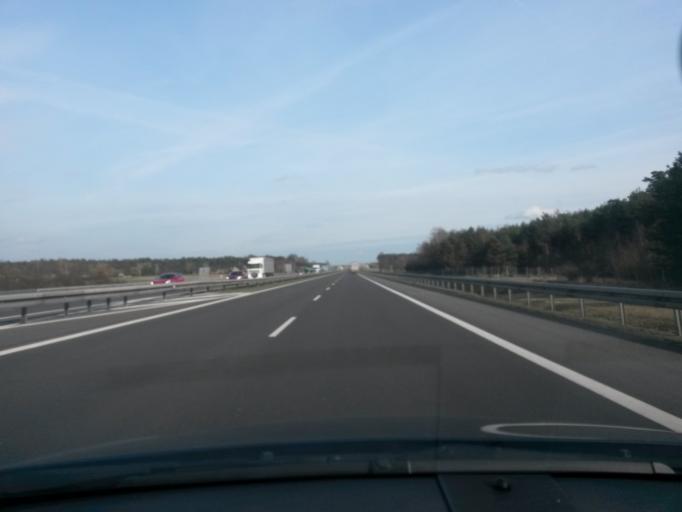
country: PL
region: Greater Poland Voivodeship
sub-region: Powiat koninski
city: Golina
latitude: 52.1772
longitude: 18.1343
